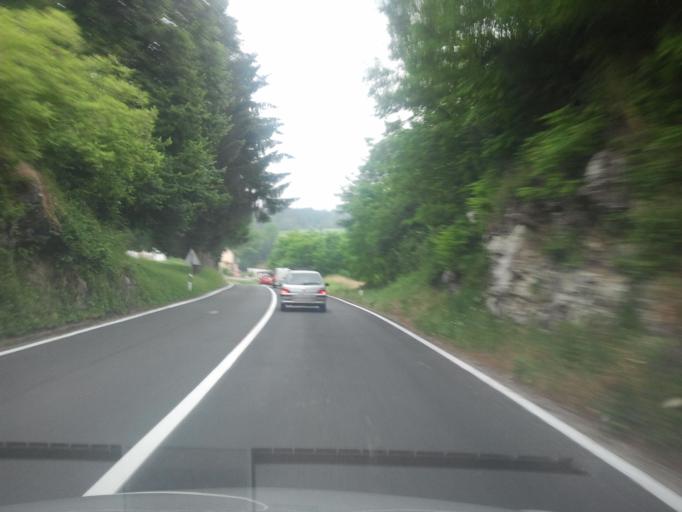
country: HR
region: Karlovacka
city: Vojnic
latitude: 45.2892
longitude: 15.5864
